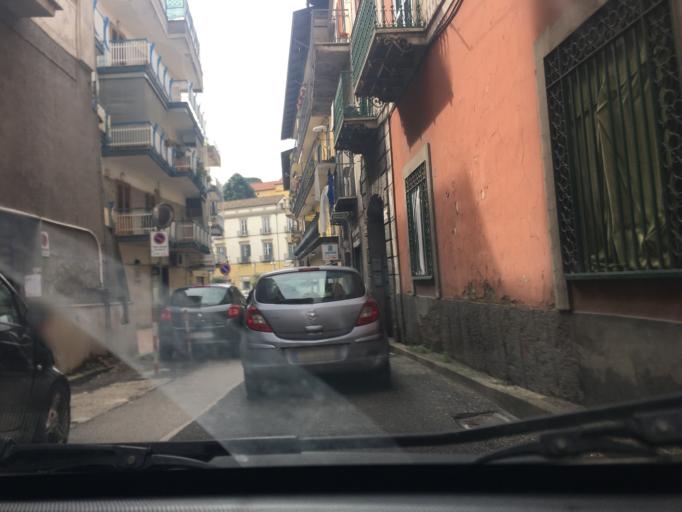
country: IT
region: Campania
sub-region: Provincia di Napoli
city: Calvizzano
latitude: 40.8953
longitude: 14.1882
